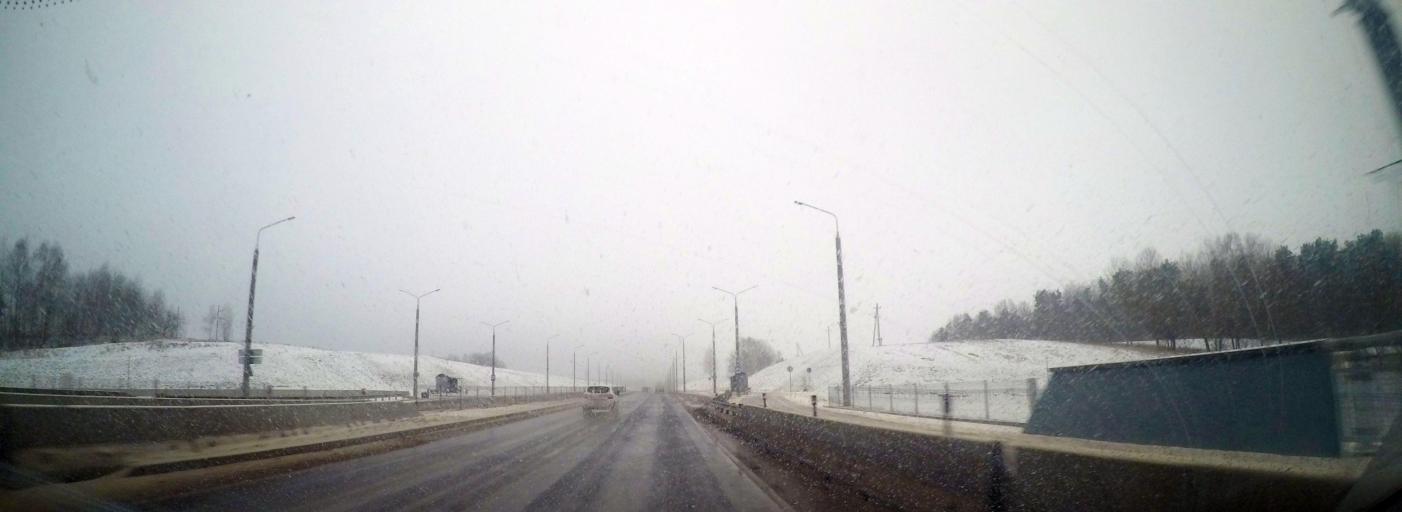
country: BY
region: Grodnenskaya
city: Hrodna
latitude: 53.6521
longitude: 23.8858
